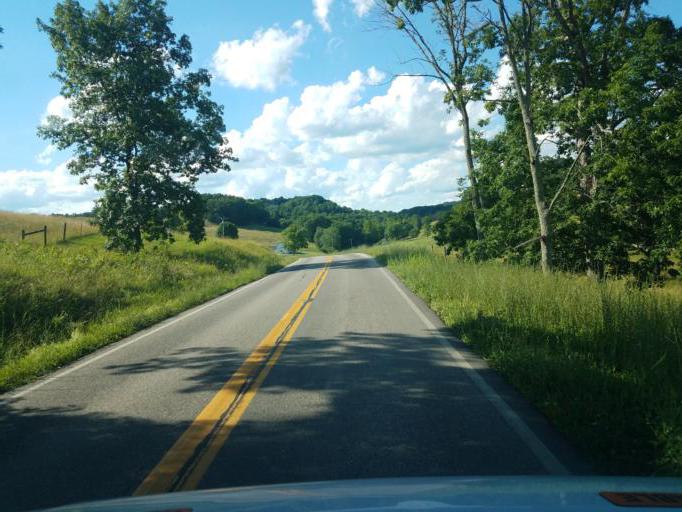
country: US
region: Ohio
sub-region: Gallia County
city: Gallipolis
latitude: 38.7616
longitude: -82.3552
